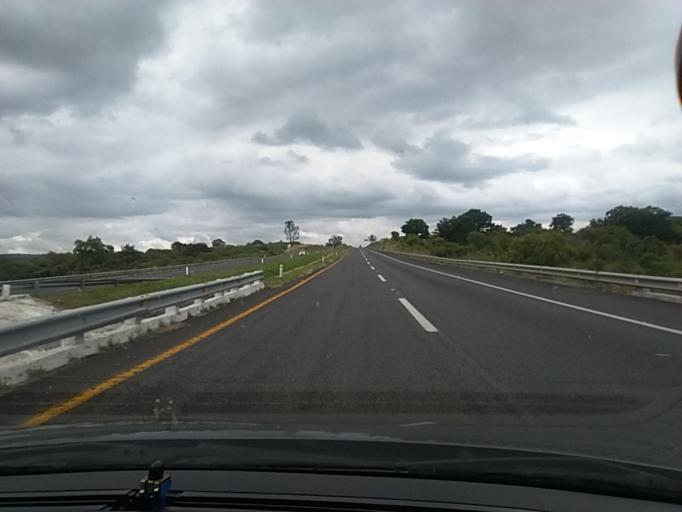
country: MX
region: Jalisco
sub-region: Zapotlanejo
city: La Mezquitera
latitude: 20.5512
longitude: -103.0448
